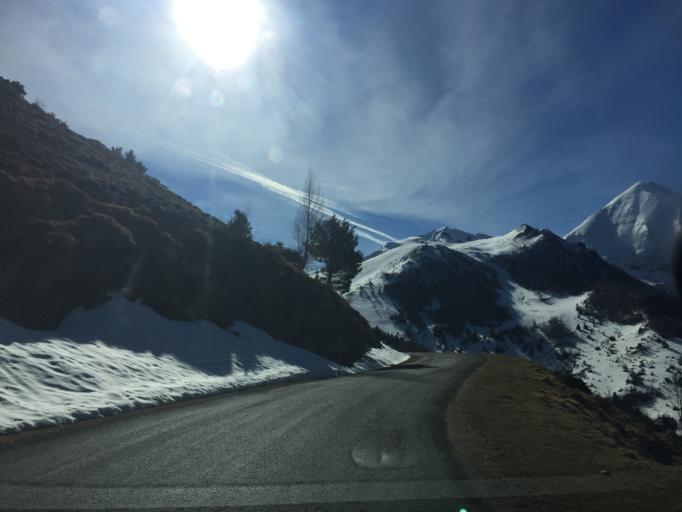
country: FR
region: Midi-Pyrenees
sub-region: Departement des Hautes-Pyrenees
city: Saint-Lary-Soulan
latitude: 42.8002
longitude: 0.3734
